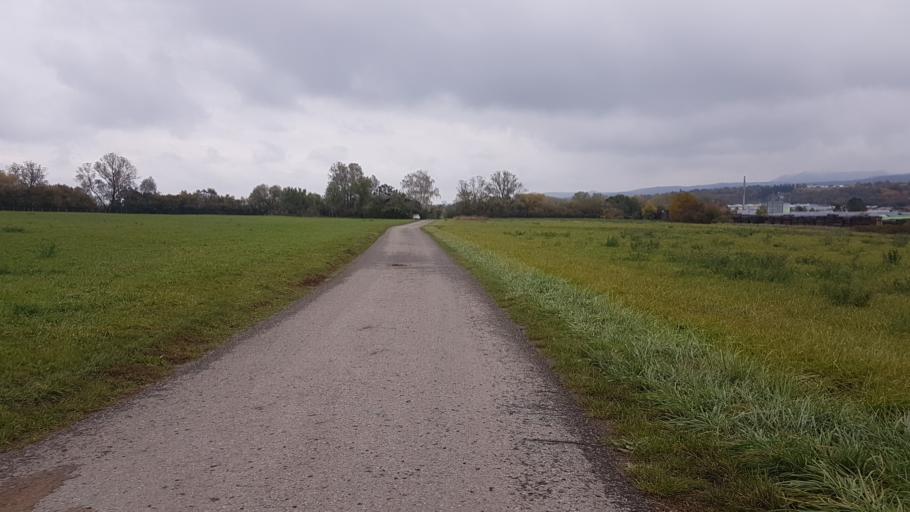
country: DE
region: Baden-Wuerttemberg
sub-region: Tuebingen Region
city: Ofterdingen
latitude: 48.4260
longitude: 9.0349
